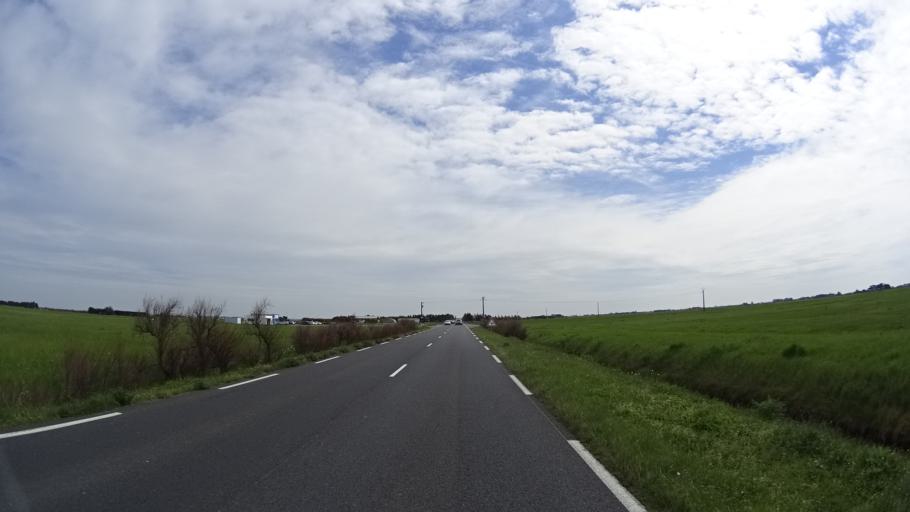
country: FR
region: Pays de la Loire
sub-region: Departement de la Vendee
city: La Barre-de-Monts
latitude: 46.8894
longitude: -2.0911
